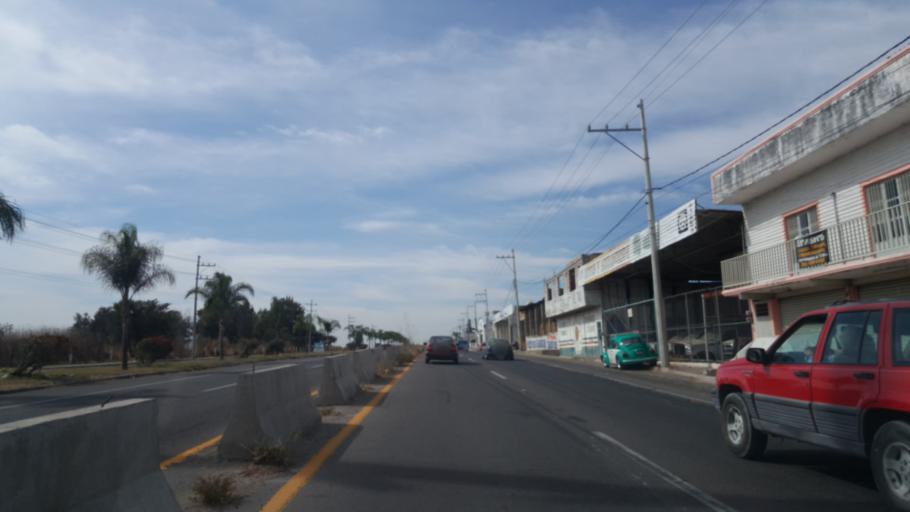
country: MX
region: Jalisco
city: San Juan de los Lagos
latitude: 21.2718
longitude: -102.3044
